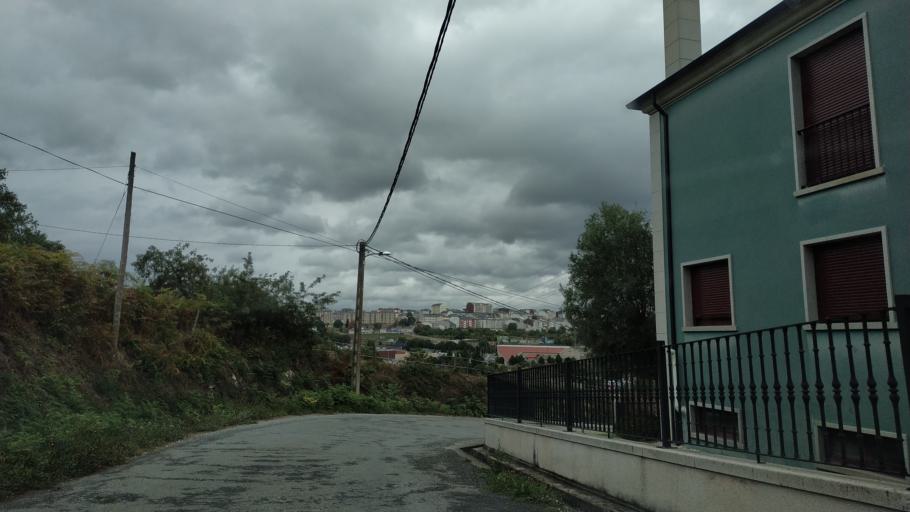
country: ES
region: Galicia
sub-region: Provincia de Lugo
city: Lugo
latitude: 42.9998
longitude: -7.5753
